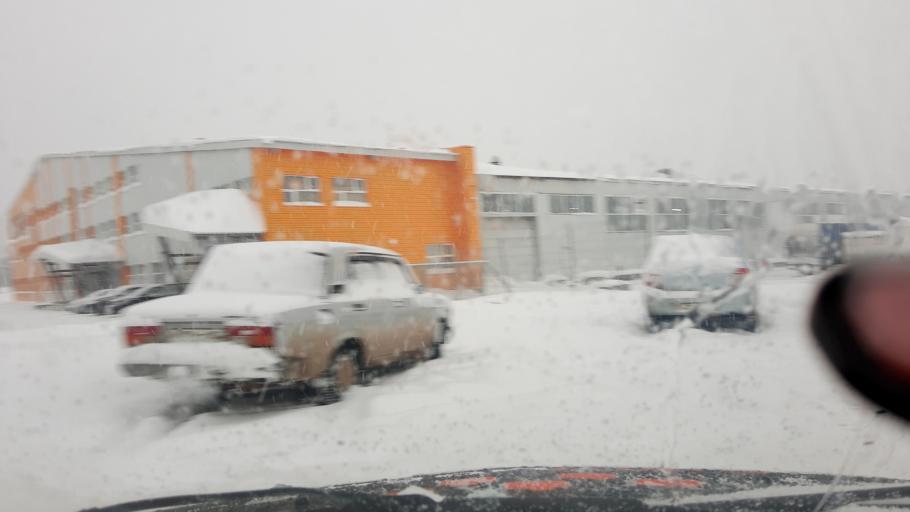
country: RU
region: Bashkortostan
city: Blagoveshchensk
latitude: 55.0291
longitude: 56.0237
